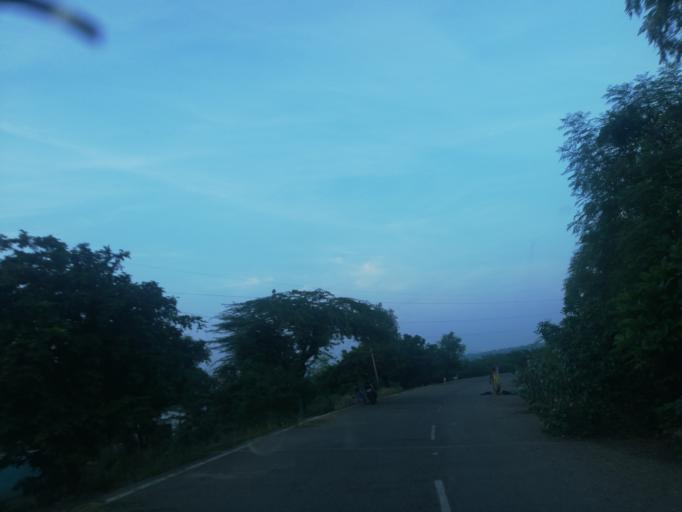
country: IN
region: Andhra Pradesh
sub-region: Guntur
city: Macherla
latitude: 16.5819
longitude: 79.3258
